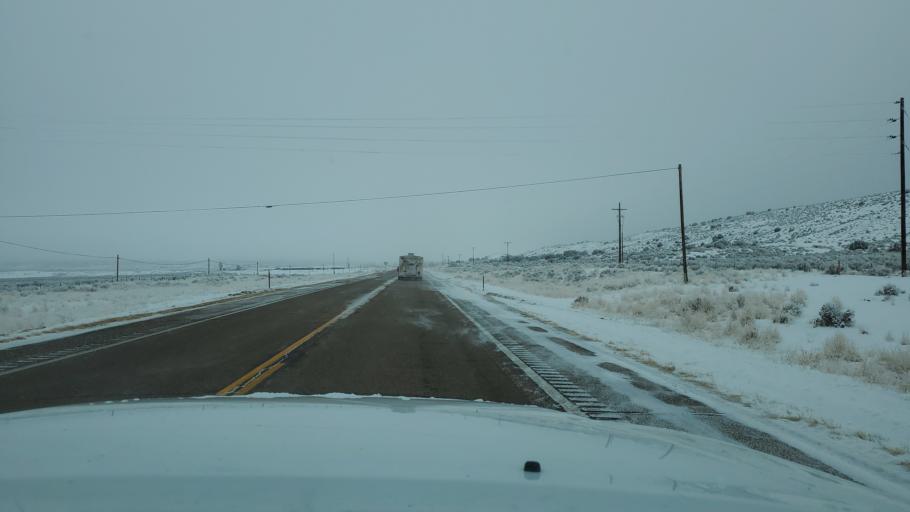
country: US
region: Colorado
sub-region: Rio Blanco County
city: Rangely
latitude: 40.2431
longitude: -108.9797
